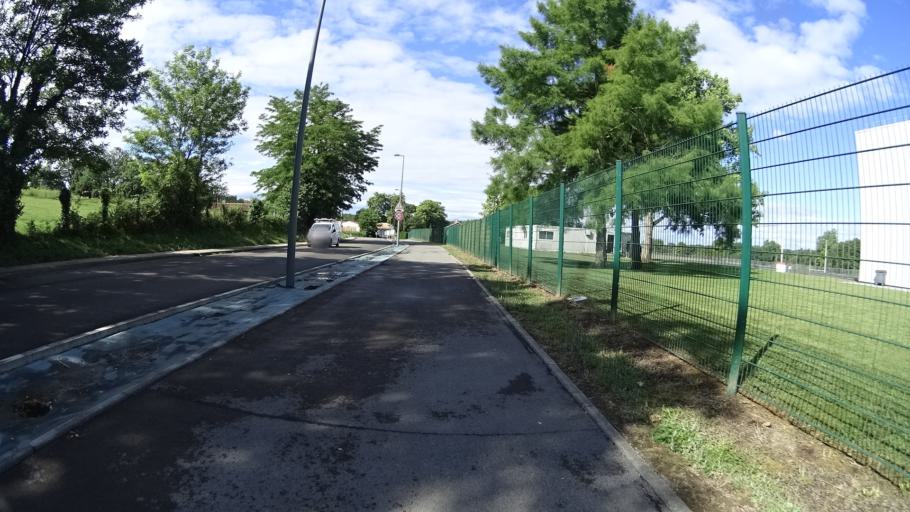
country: FR
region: Aquitaine
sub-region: Departement des Landes
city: Oeyreluy
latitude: 43.6932
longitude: -1.0817
